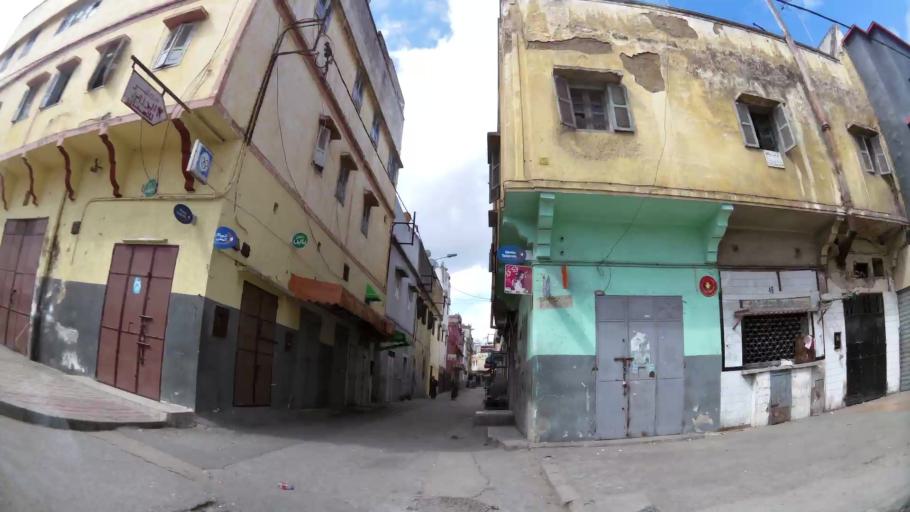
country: MA
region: Gharb-Chrarda-Beni Hssen
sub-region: Kenitra Province
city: Kenitra
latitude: 34.2660
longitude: -6.5617
